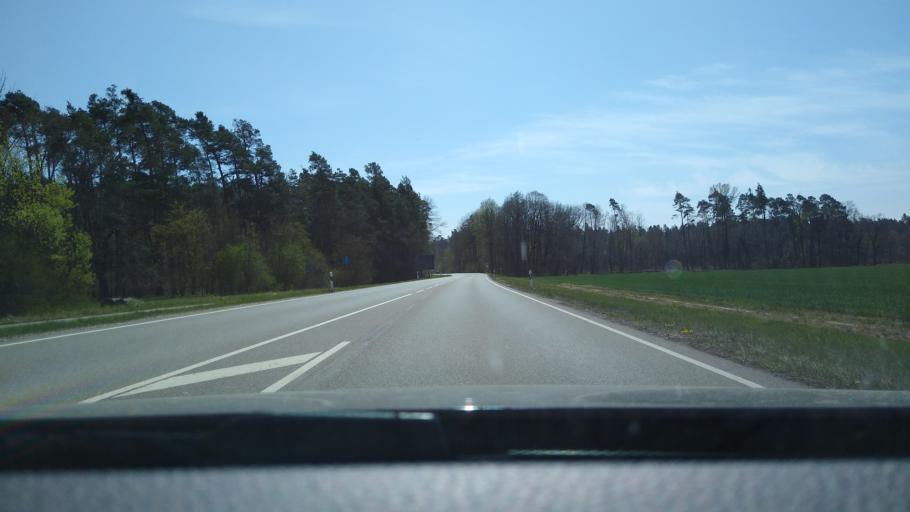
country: DE
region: Bavaria
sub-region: Regierungsbezirk Mittelfranken
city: Merkendorf
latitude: 49.1832
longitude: 10.7156
